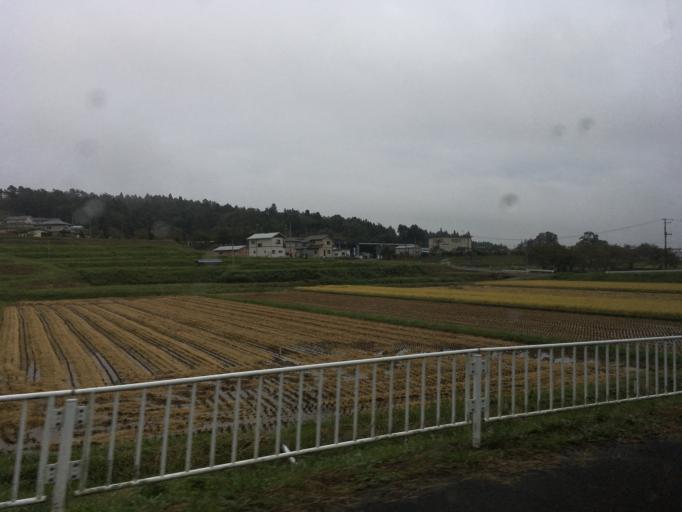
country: JP
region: Iwate
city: Ichinoseki
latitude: 38.8324
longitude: 141.2039
